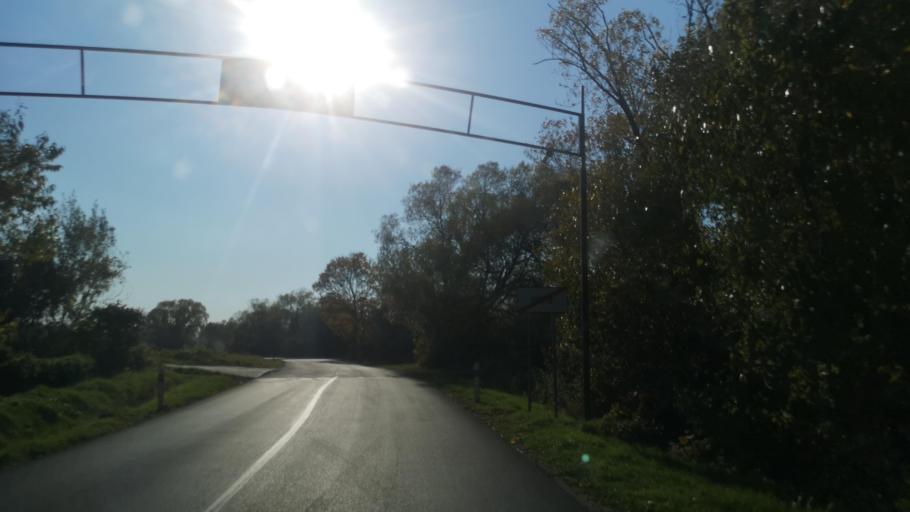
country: SK
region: Nitriansky
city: Zlate Moravce
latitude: 48.4442
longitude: 18.4334
